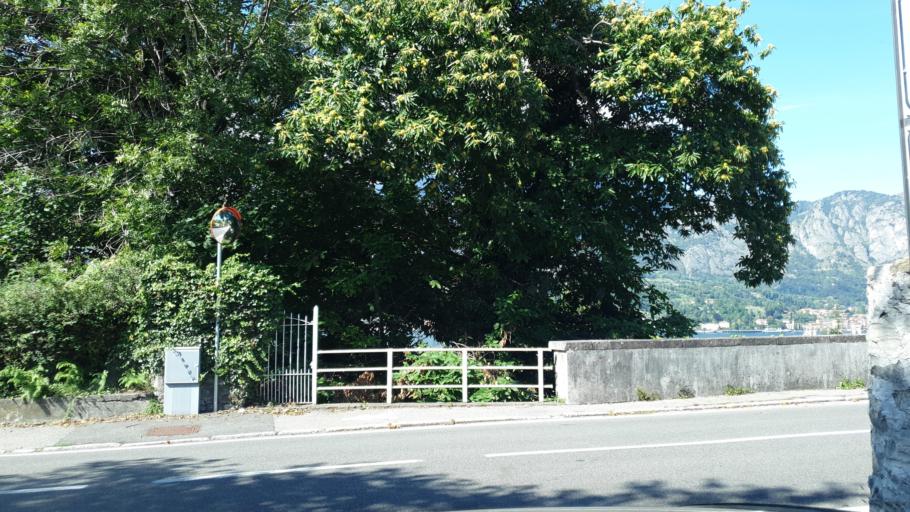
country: IT
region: Lombardy
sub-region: Provincia di Como
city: Bellagio
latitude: 45.9779
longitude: 9.2544
